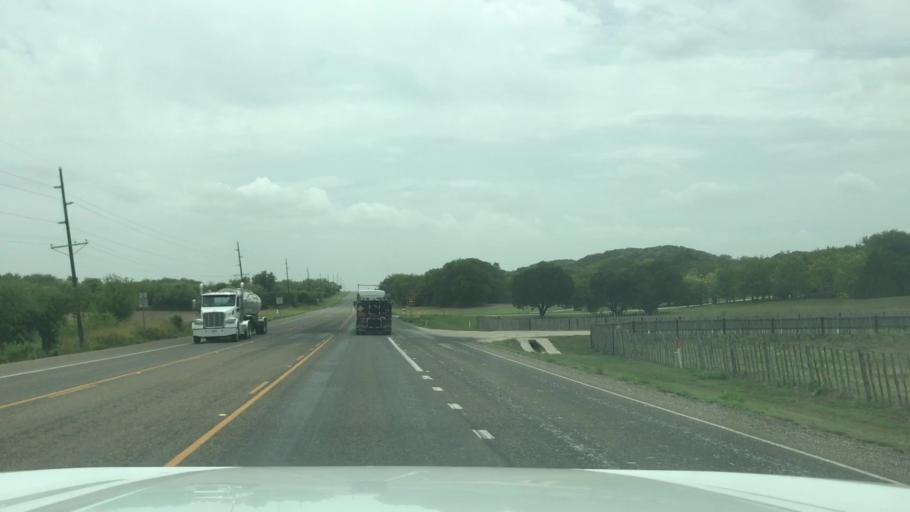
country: US
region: Texas
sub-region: Bosque County
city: Clifton
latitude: 31.7274
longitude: -97.5496
